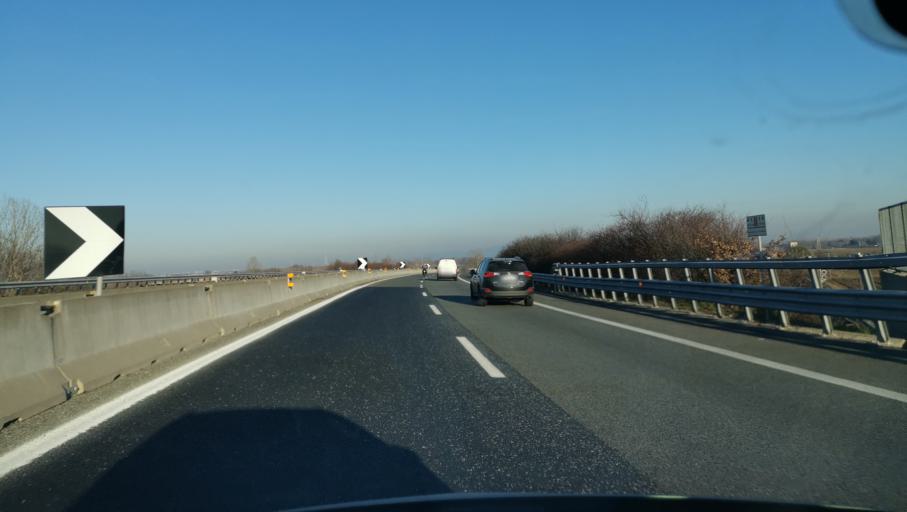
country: IT
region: Piedmont
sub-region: Provincia di Torino
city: Airasca
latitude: 44.9245
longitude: 7.4583
